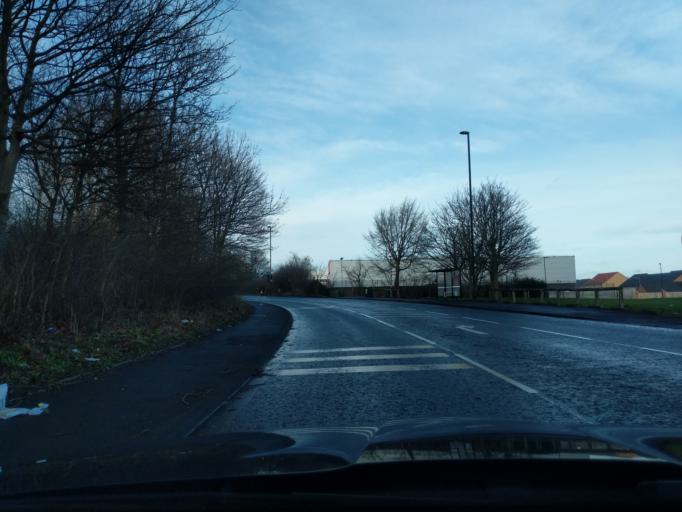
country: GB
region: England
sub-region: Gateshead
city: Felling
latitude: 54.9758
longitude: -1.5710
